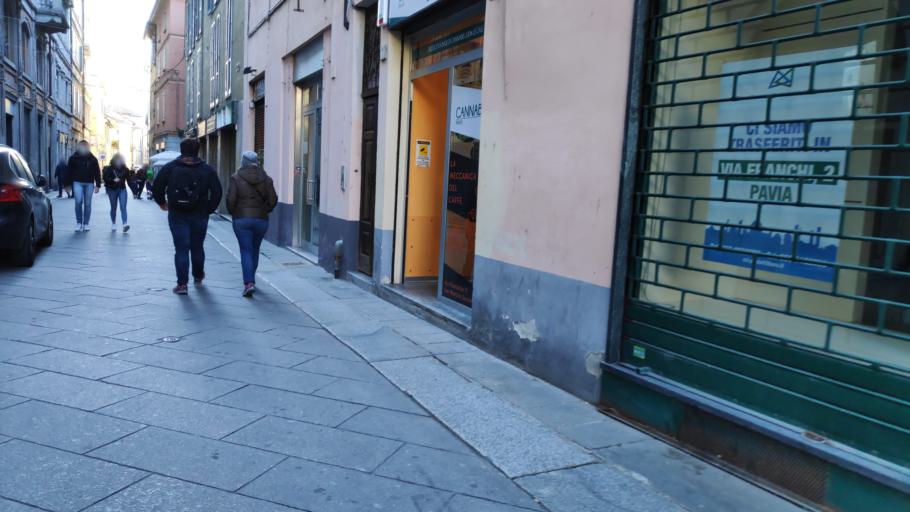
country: IT
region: Lombardy
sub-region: Provincia di Pavia
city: Pavia
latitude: 45.1863
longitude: 9.1546
